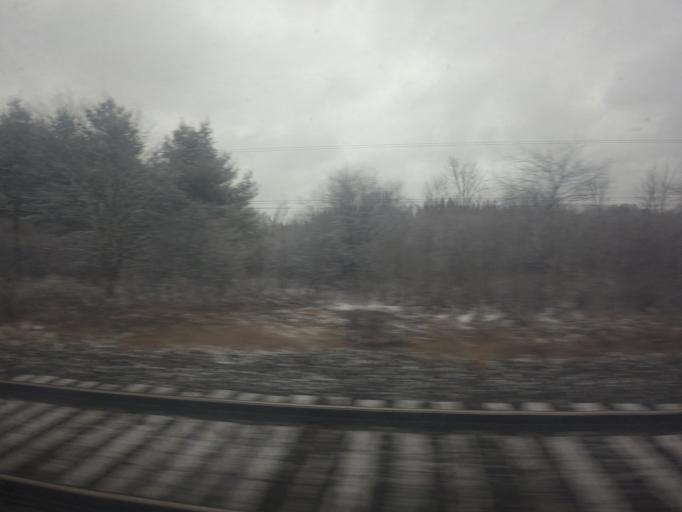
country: US
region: New York
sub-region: Jefferson County
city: Alexandria Bay
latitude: 44.4225
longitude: -75.9852
